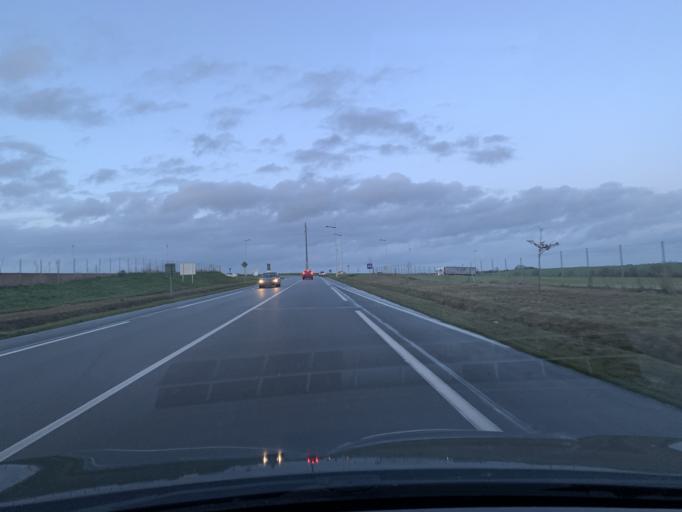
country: FR
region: Nord-Pas-de-Calais
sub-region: Departement du Nord
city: Escaudoeuvres
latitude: 50.1584
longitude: 3.2983
